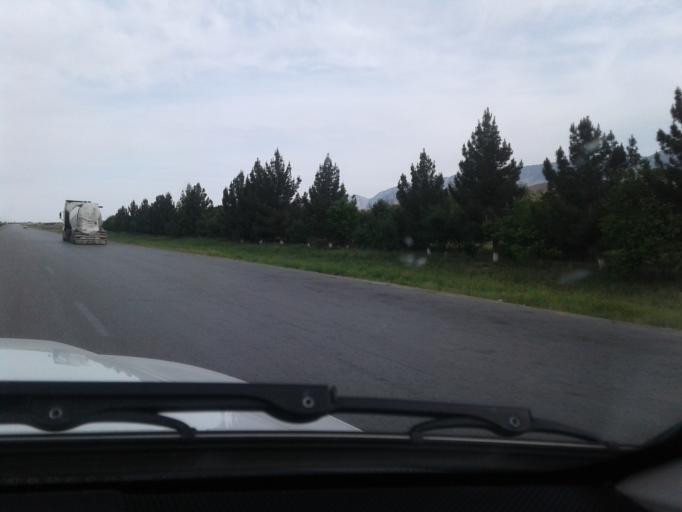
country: TM
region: Ahal
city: Baharly
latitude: 38.2424
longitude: 57.7635
